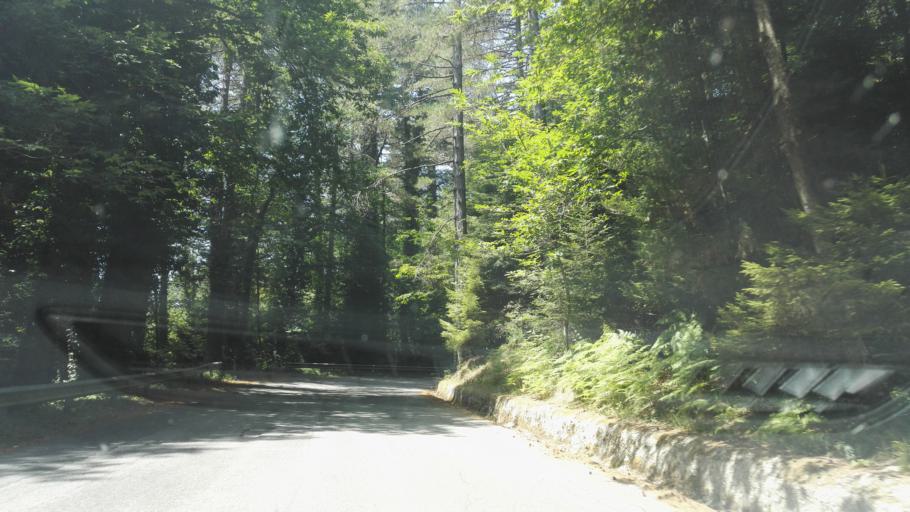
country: IT
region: Calabria
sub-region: Provincia di Vibo-Valentia
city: Mongiana
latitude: 38.5188
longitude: 16.3203
